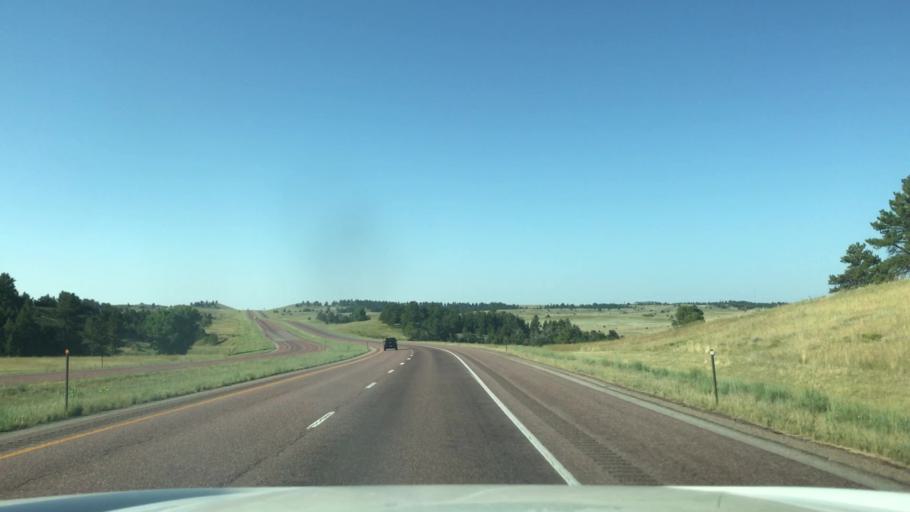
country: US
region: Wyoming
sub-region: Platte County
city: Guernsey
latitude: 42.4224
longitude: -105.0392
